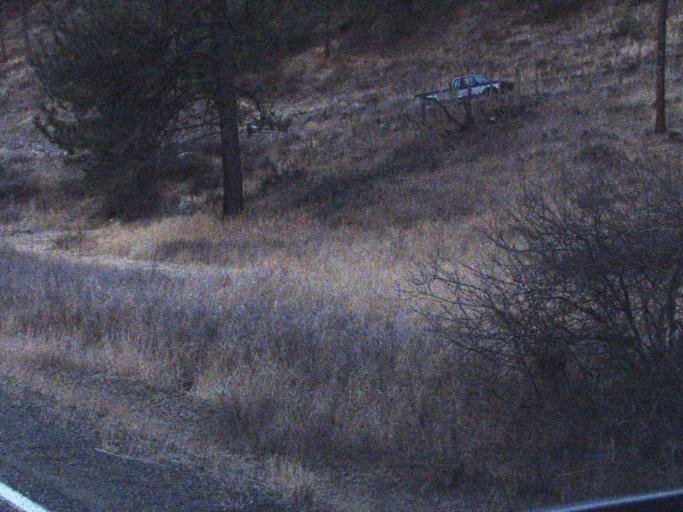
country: US
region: Washington
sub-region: Ferry County
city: Republic
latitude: 48.5694
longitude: -118.7479
